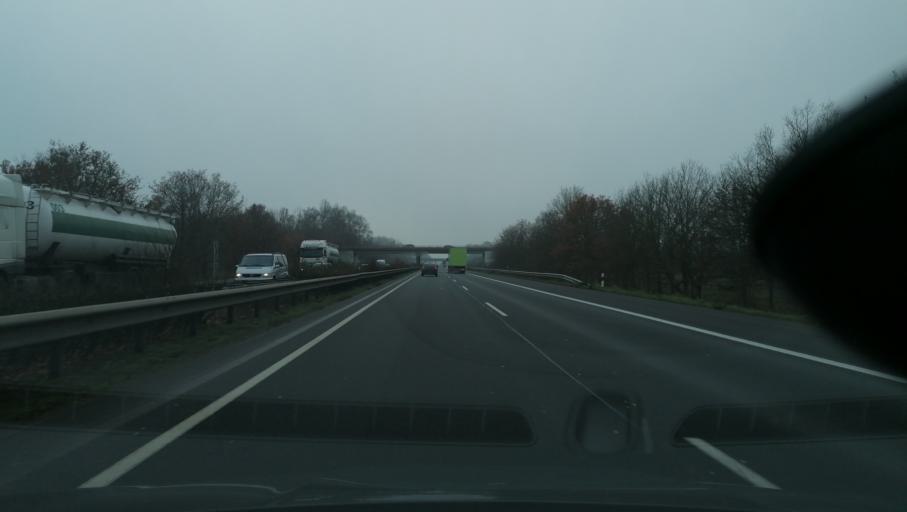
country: DE
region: Lower Saxony
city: Dinklage
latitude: 52.6401
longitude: 8.1511
